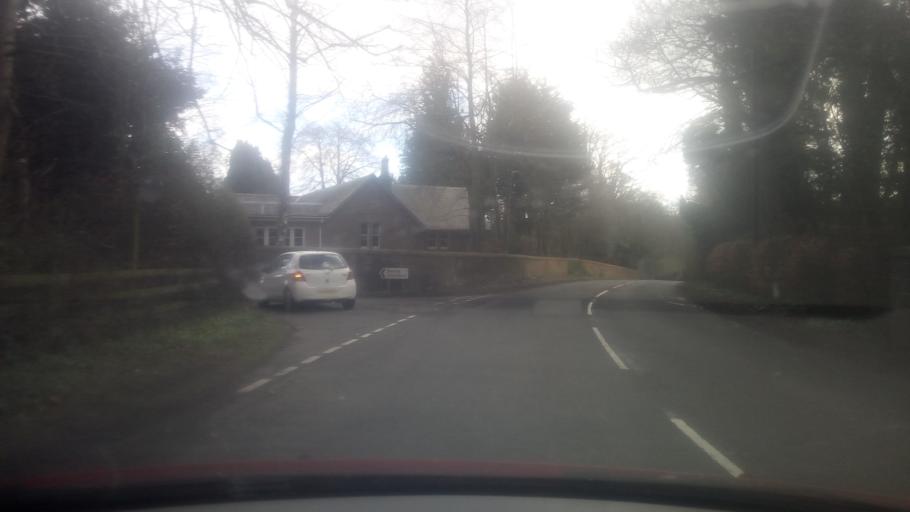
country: GB
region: Scotland
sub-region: The Scottish Borders
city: Saint Boswells
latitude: 55.5658
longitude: -2.6315
